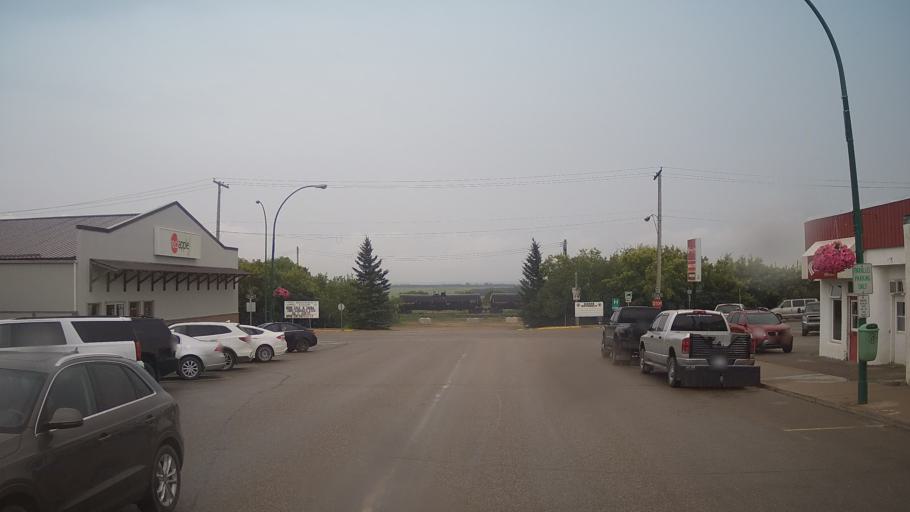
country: CA
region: Saskatchewan
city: Biggar
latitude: 52.0545
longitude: -107.9862
